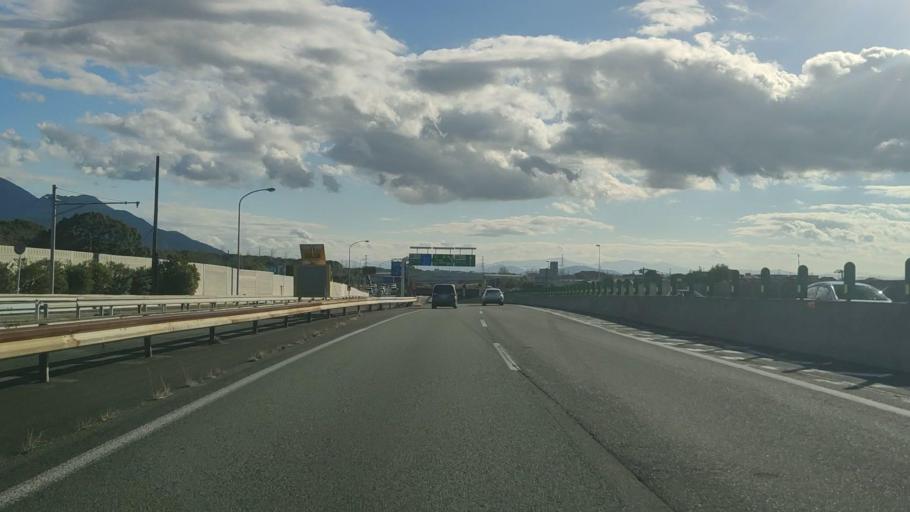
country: JP
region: Fukuoka
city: Nakama
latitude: 33.7954
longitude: 130.7440
